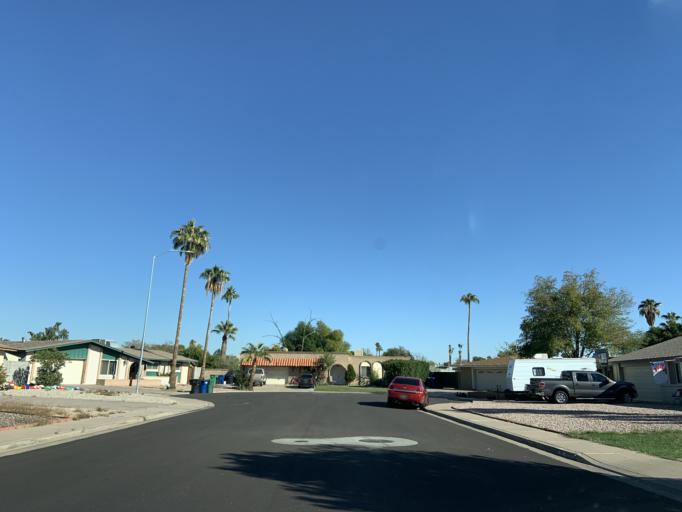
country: US
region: Arizona
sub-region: Maricopa County
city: Tempe
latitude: 33.4027
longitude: -111.8799
